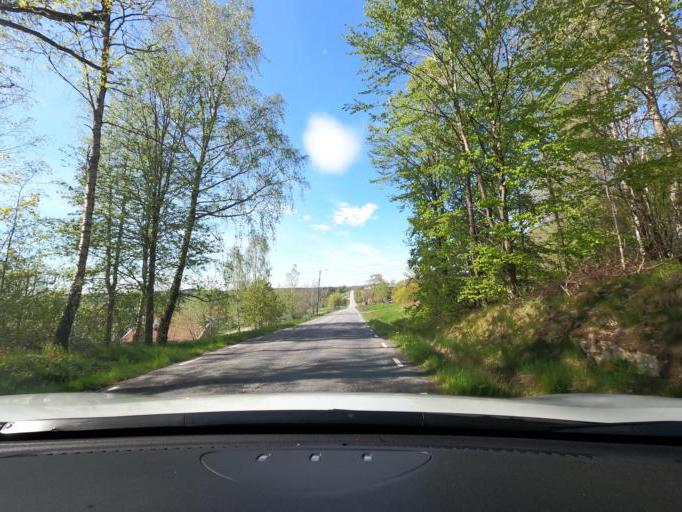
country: SE
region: Vaestra Goetaland
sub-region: Marks Kommun
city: Bua
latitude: 57.5006
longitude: 12.5525
